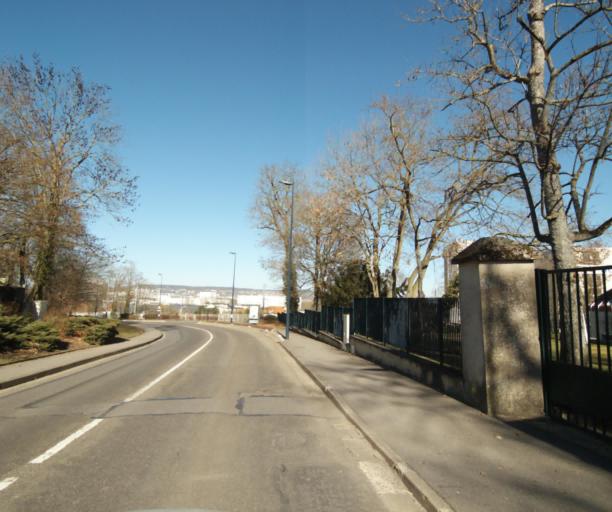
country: FR
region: Lorraine
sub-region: Departement de Meurthe-et-Moselle
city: Jarville-la-Malgrange
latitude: 48.6666
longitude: 6.2084
